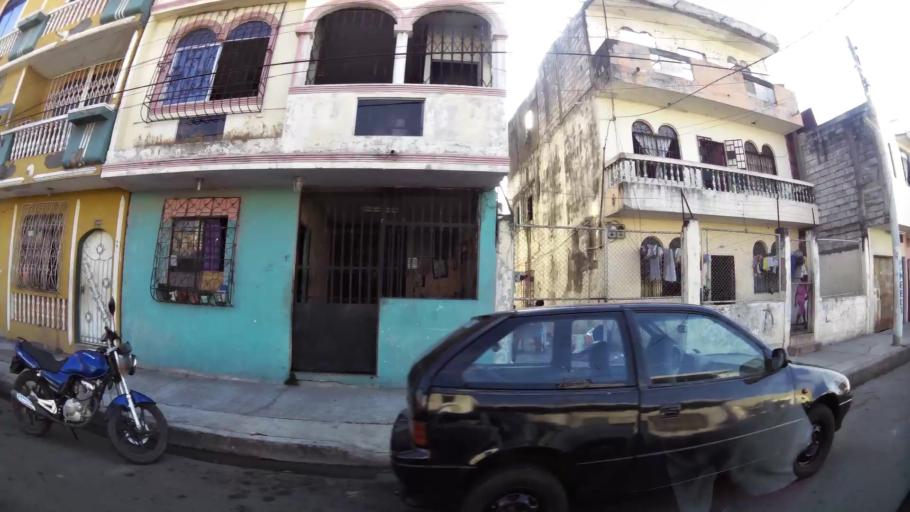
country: EC
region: Guayas
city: Guayaquil
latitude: -2.2179
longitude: -79.9087
